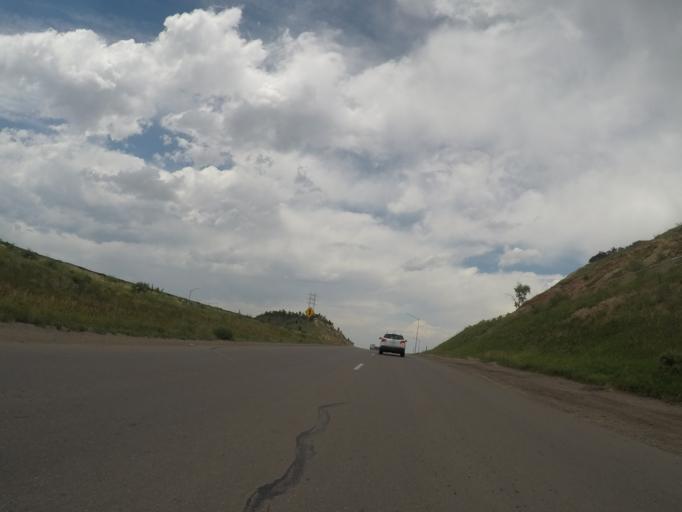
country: US
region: Colorado
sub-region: Jefferson County
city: West Pleasant View
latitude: 39.6994
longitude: -105.2037
